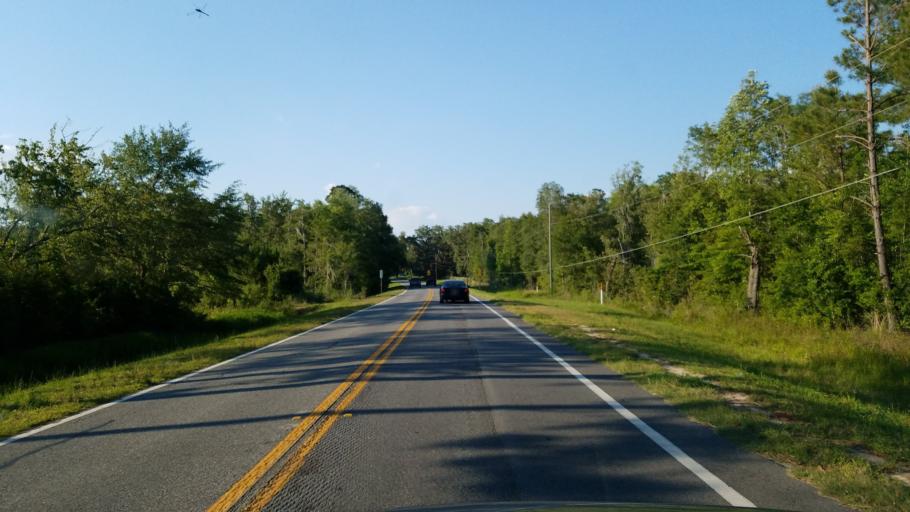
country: US
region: Georgia
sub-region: Lanier County
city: Lakeland
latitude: 31.0037
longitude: -83.0660
